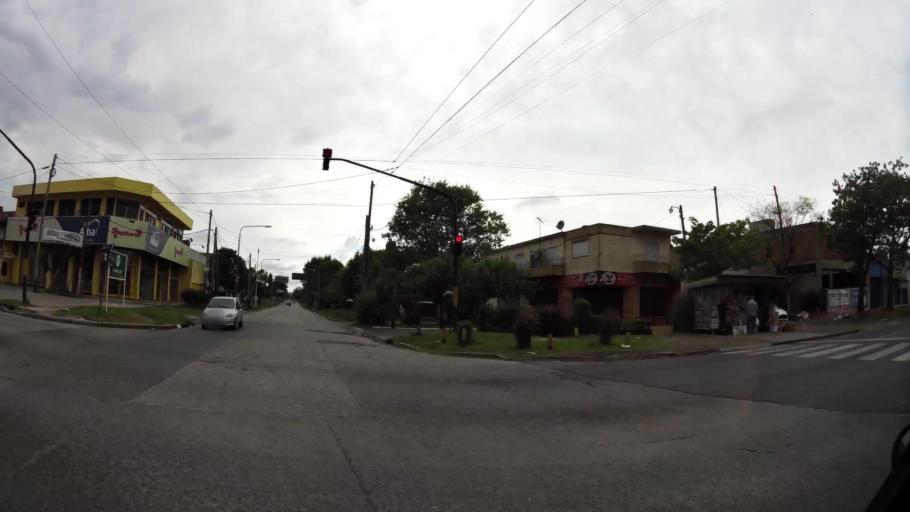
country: AR
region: Buenos Aires
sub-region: Partido de Quilmes
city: Quilmes
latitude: -34.7649
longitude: -58.2852
